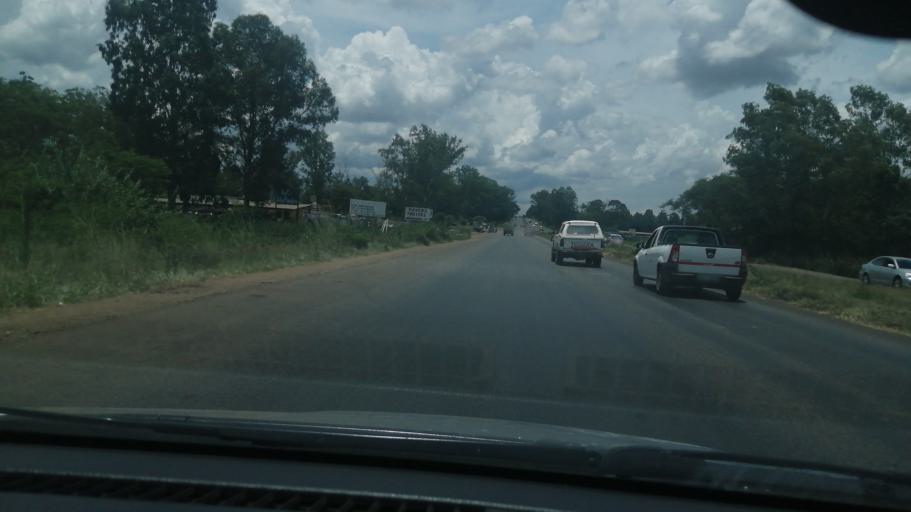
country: ZW
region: Harare
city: Harare
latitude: -17.8217
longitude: 30.9575
